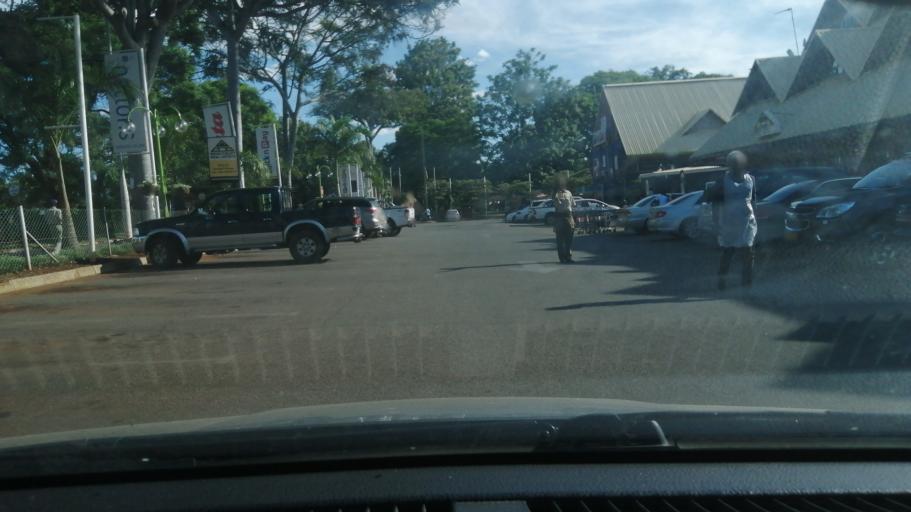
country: ZW
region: Harare
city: Harare
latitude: -17.7629
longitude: 31.0516
